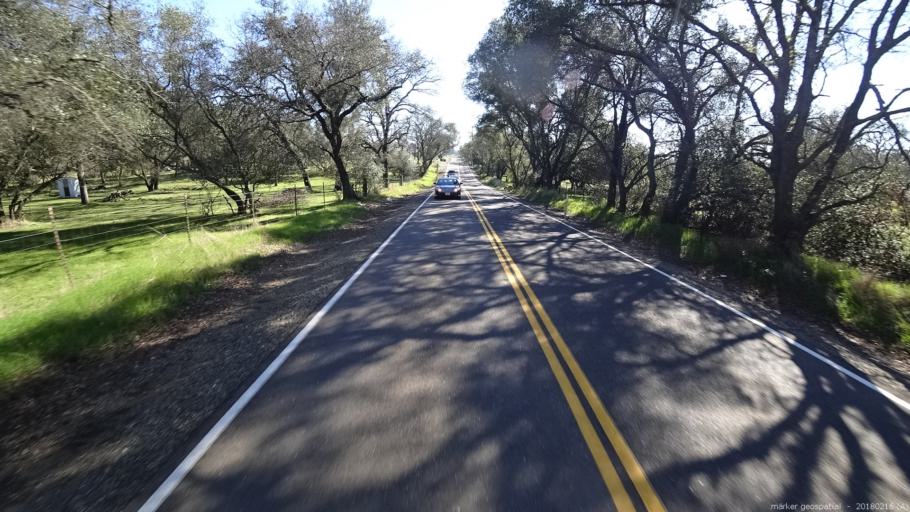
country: US
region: California
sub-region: Sacramento County
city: Rancho Murieta
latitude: 38.5283
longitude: -121.1041
